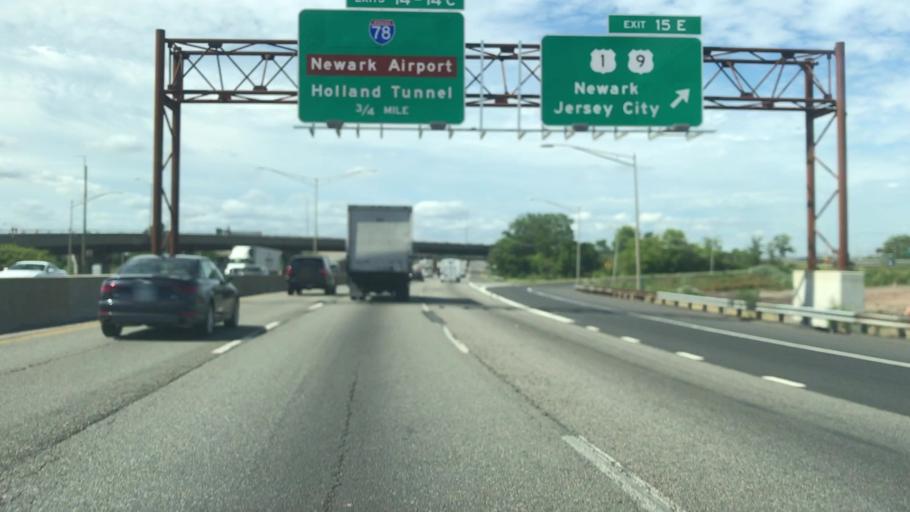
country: US
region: New Jersey
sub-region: Hudson County
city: Harrison
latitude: 40.7320
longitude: -74.1267
